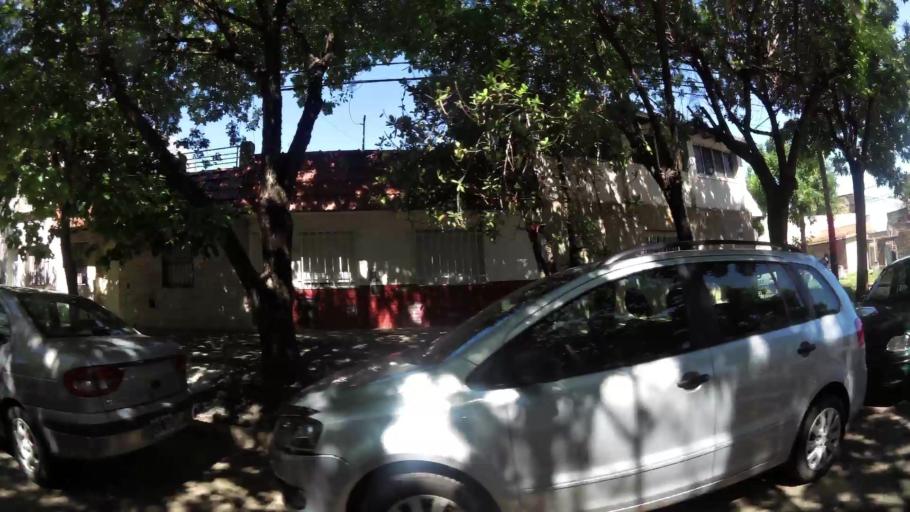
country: AR
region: Santa Fe
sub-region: Departamento de Rosario
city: Rosario
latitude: -32.9451
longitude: -60.6877
